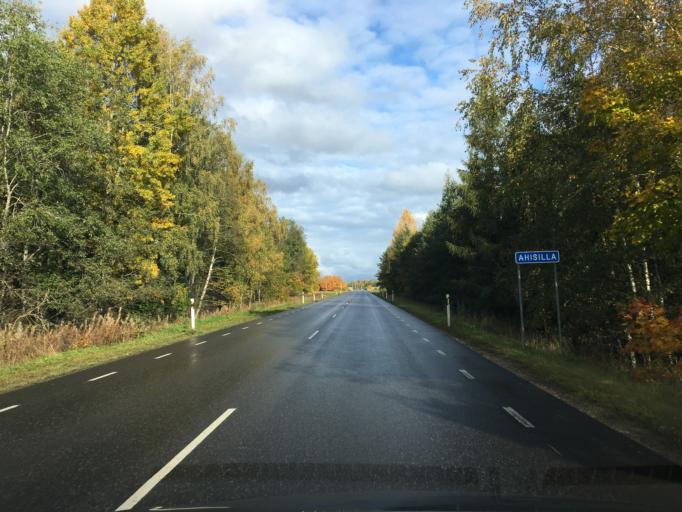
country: EE
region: Harju
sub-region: Raasiku vald
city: Raasiku
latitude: 59.1966
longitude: 25.1848
